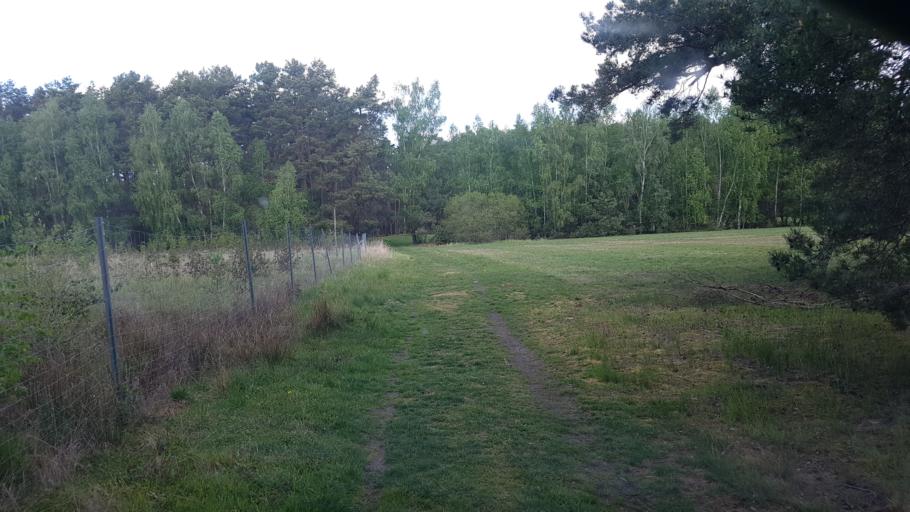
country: DE
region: Brandenburg
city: Finsterwalde
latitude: 51.6435
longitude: 13.6613
